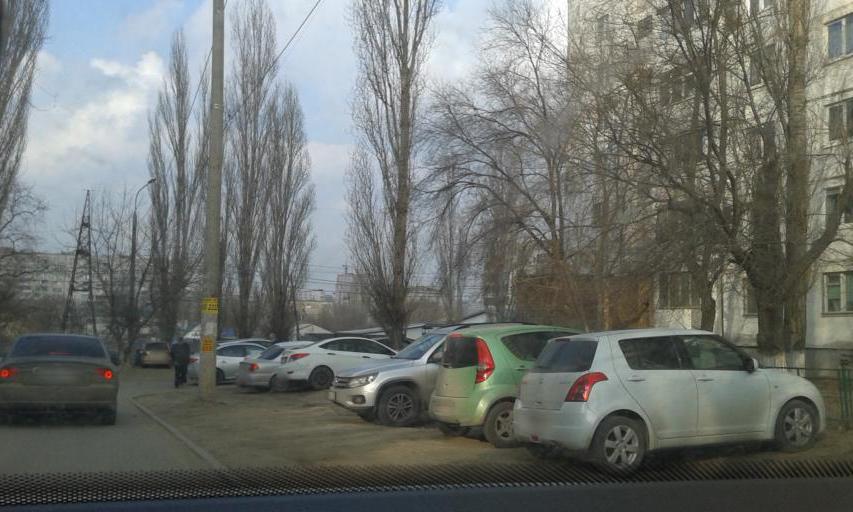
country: RU
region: Volgograd
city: Volgograd
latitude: 48.6549
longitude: 44.4335
